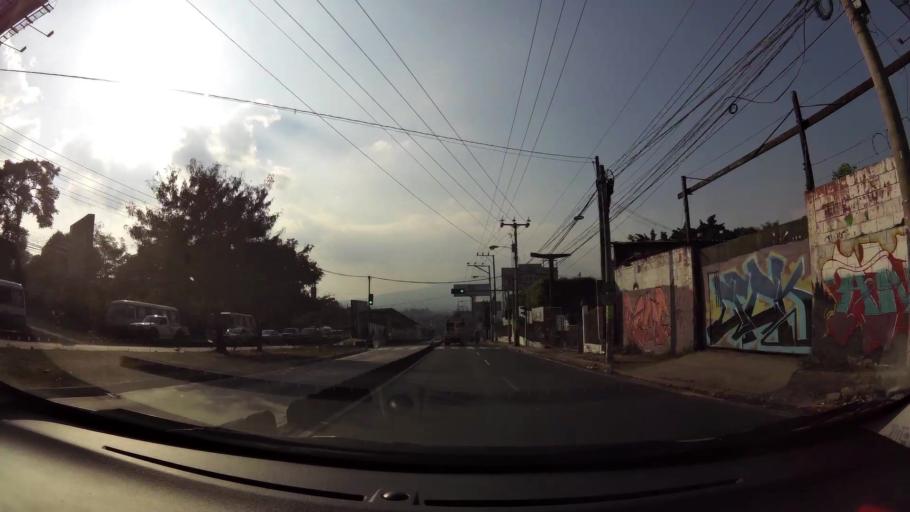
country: SV
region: San Salvador
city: Soyapango
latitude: 13.7009
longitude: -89.1551
